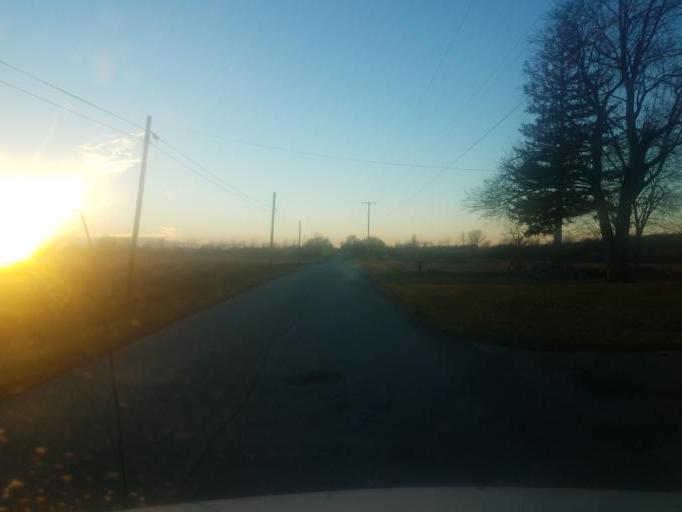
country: US
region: Ohio
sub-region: Richland County
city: Ontario
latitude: 40.8431
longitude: -82.5660
